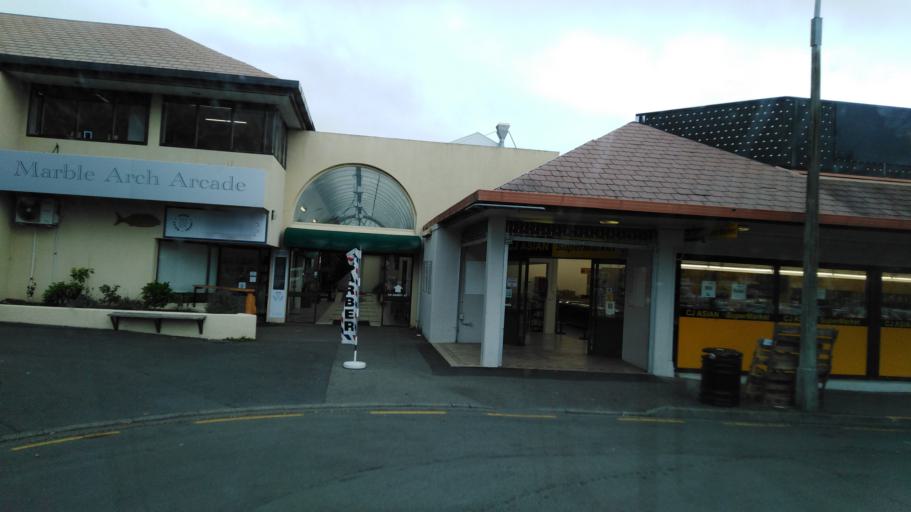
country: NZ
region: Nelson
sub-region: Nelson City
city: Nelson
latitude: -41.2737
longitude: 173.2832
